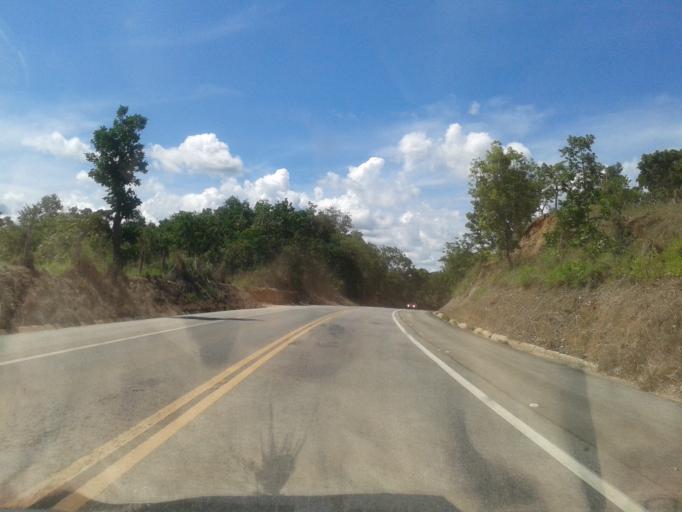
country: BR
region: Goias
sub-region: Goias
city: Goias
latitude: -15.6692
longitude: -50.2151
